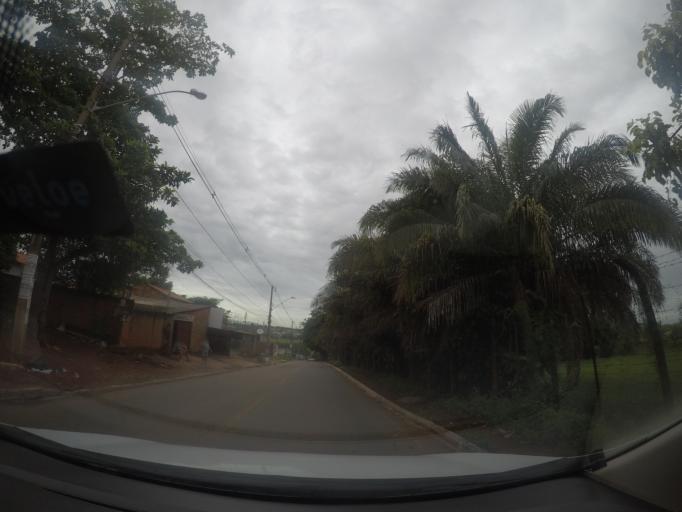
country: BR
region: Goias
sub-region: Goiania
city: Goiania
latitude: -16.6295
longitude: -49.3074
